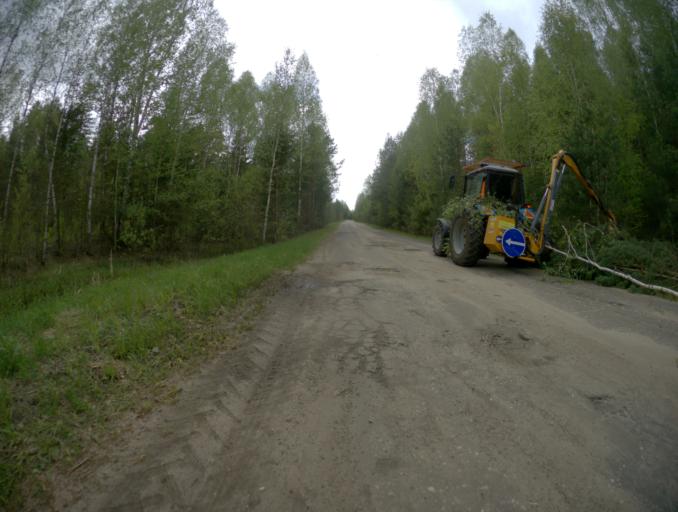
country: RU
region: Vladimir
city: Velikodvorskiy
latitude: 55.2452
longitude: 40.7078
